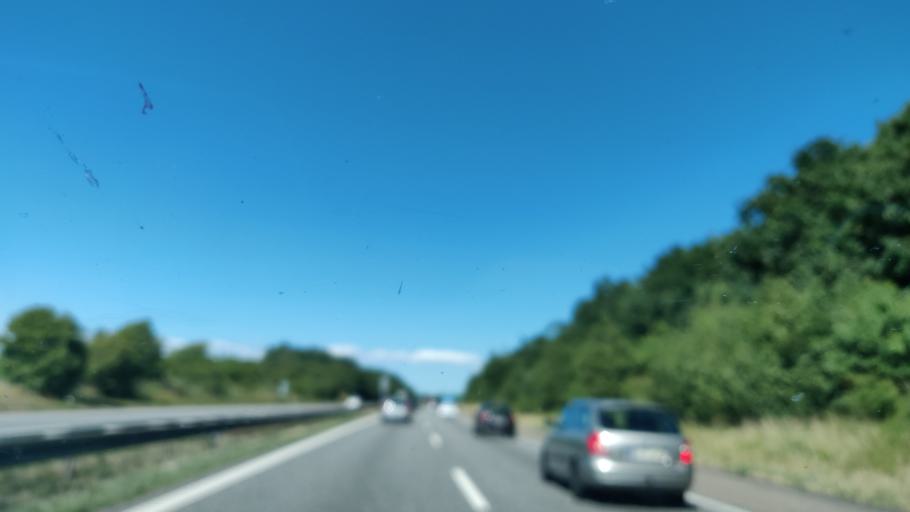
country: DK
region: Central Jutland
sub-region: Arhus Kommune
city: Framlev
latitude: 56.1384
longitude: 10.0378
